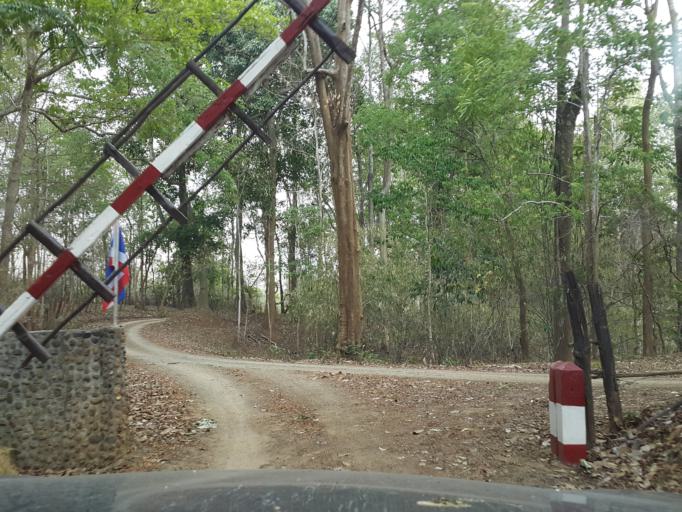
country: TH
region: Lamphun
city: Li
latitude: 17.6124
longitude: 98.9592
